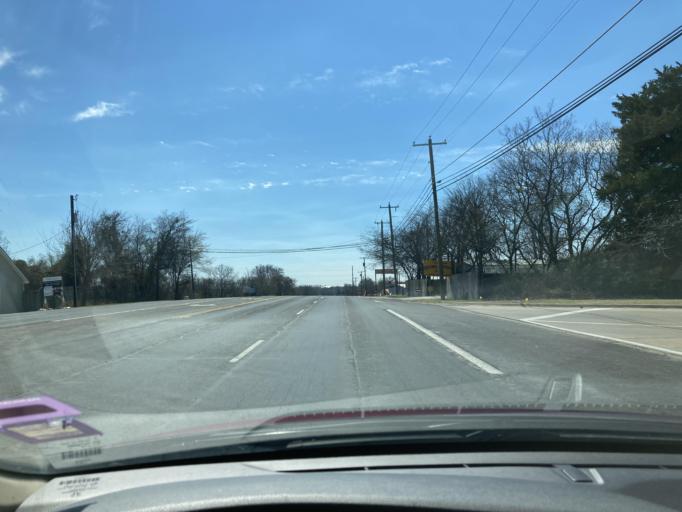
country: US
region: Texas
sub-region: Navarro County
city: Corsicana
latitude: 32.1153
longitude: -96.4647
